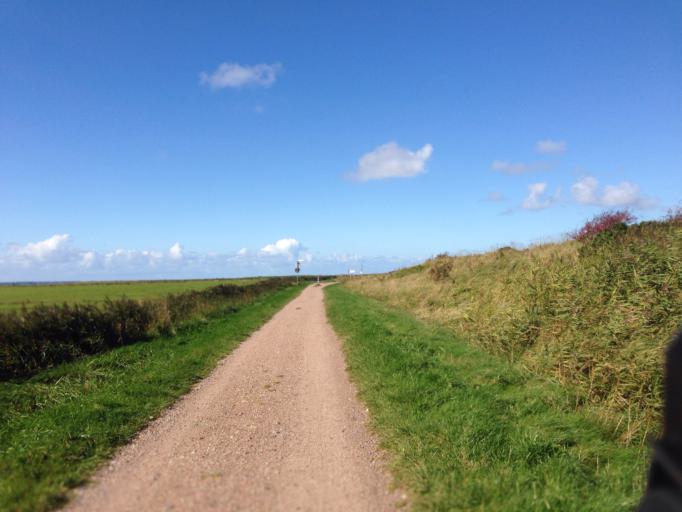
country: DE
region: Schleswig-Holstein
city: Borgsum
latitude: 54.6945
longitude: 8.4526
